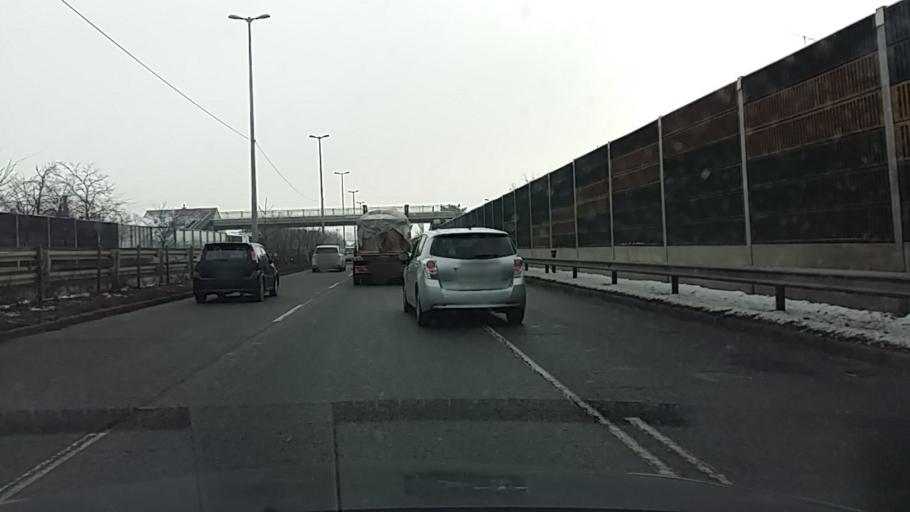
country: HU
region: Budapest
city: Budapest XIX. keruelet
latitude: 47.4444
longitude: 19.1295
